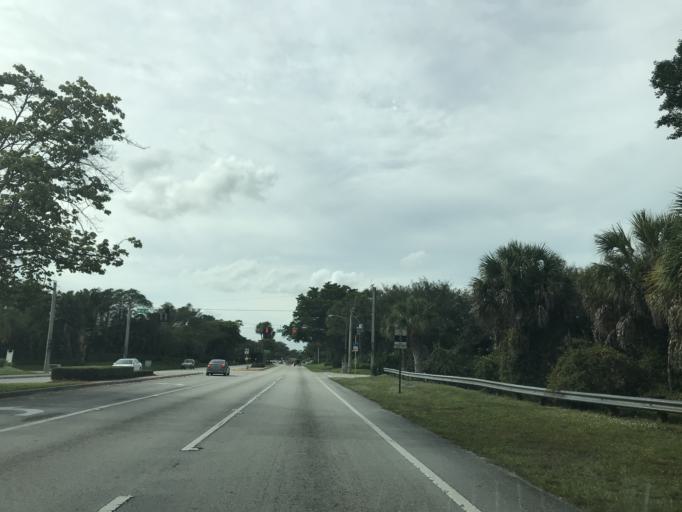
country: US
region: Florida
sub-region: Broward County
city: Coconut Creek
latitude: 26.2598
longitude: -80.1816
